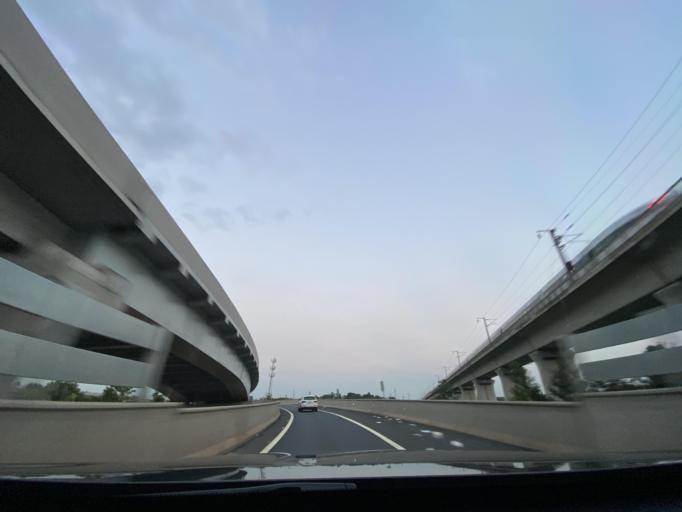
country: CN
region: Sichuan
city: Chengdu
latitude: 30.5711
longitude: 104.1367
